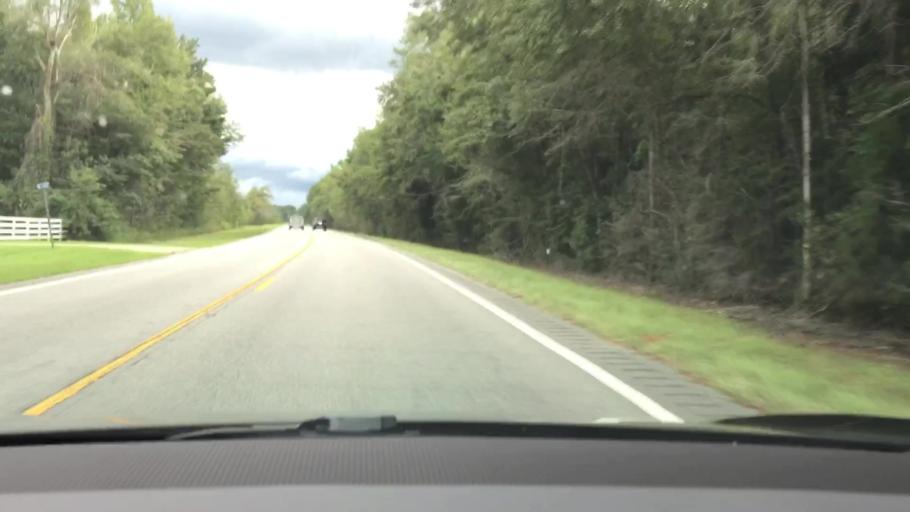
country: US
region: Alabama
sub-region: Coffee County
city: Elba
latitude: 31.4997
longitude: -86.0527
